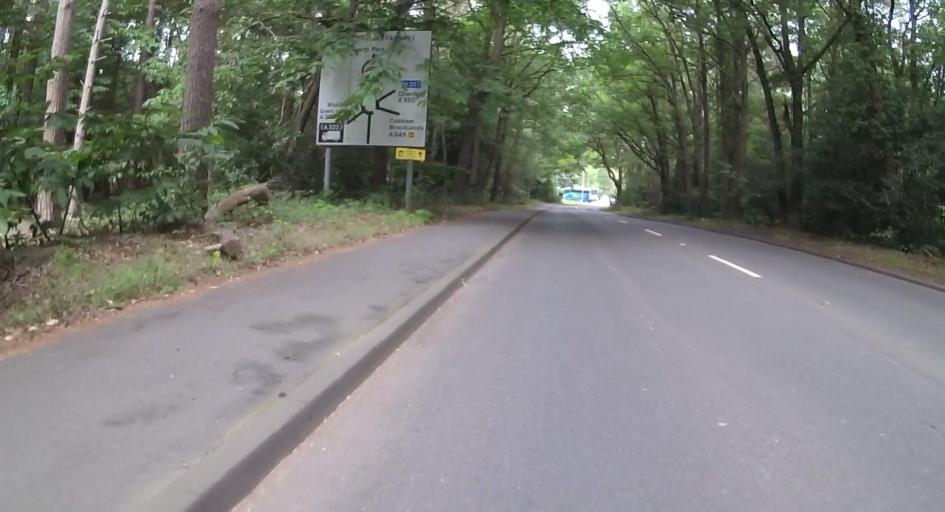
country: GB
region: England
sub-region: Surrey
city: Woking
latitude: 51.3316
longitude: -0.5450
